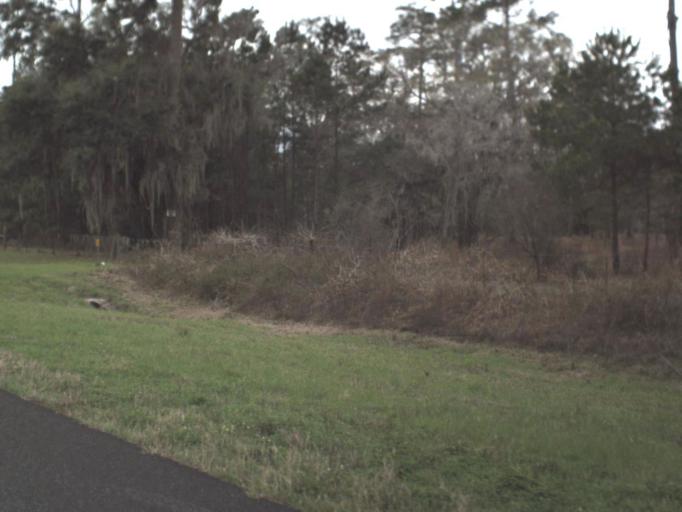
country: US
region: Florida
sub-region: Leon County
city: Tallahassee
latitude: 30.6021
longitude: -84.1828
